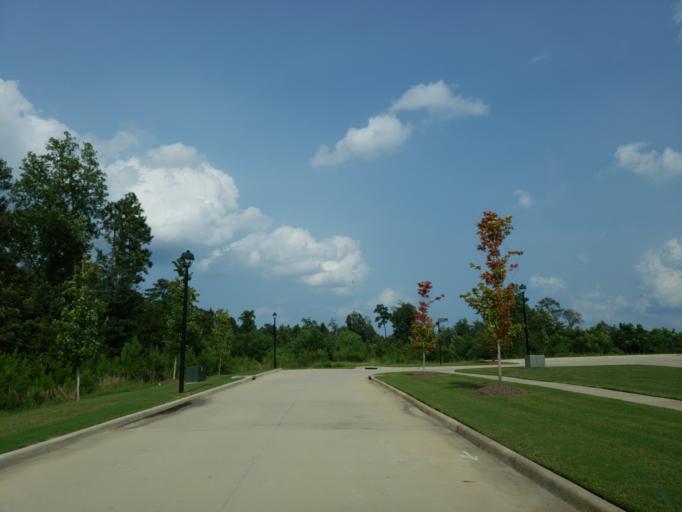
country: US
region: Mississippi
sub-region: Forrest County
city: Hattiesburg
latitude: 31.2769
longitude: -89.3225
